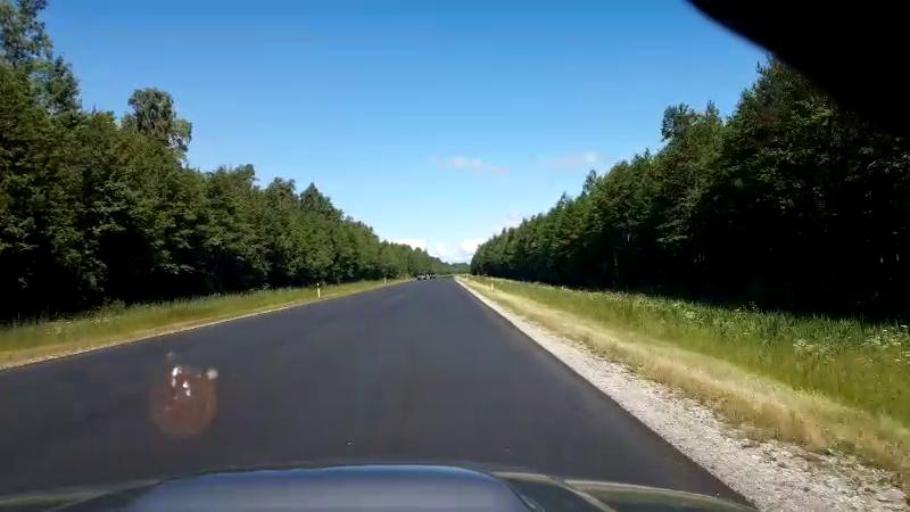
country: LV
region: Salacgrivas
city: Ainazi
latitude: 57.9319
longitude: 24.4271
